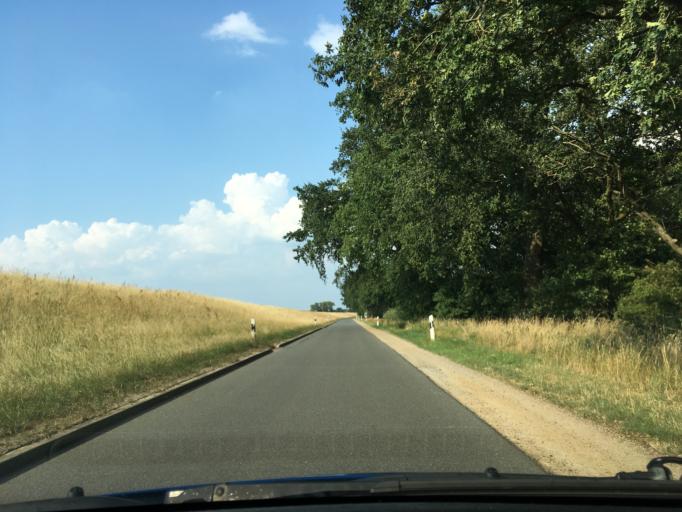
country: DE
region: Lower Saxony
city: Damnatz
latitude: 53.1502
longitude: 11.1220
